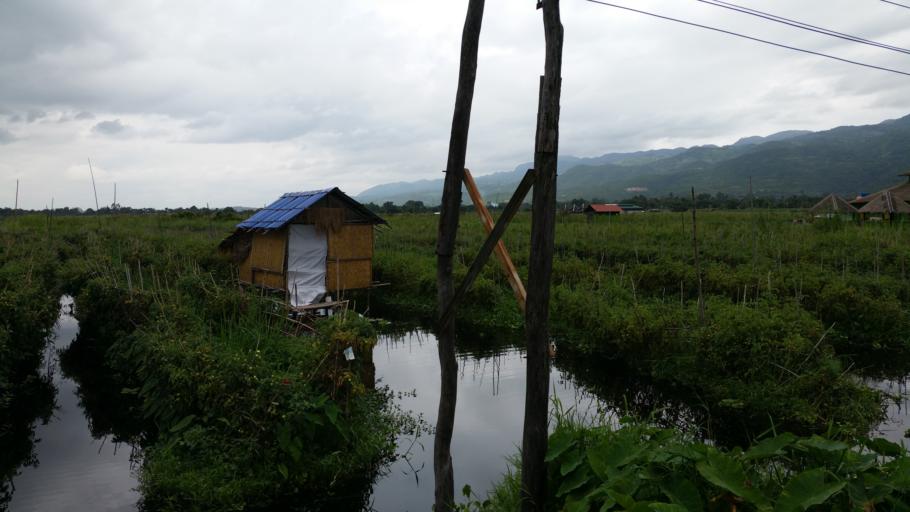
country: MM
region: Shan
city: Taunggyi
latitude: 20.5812
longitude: 96.9354
